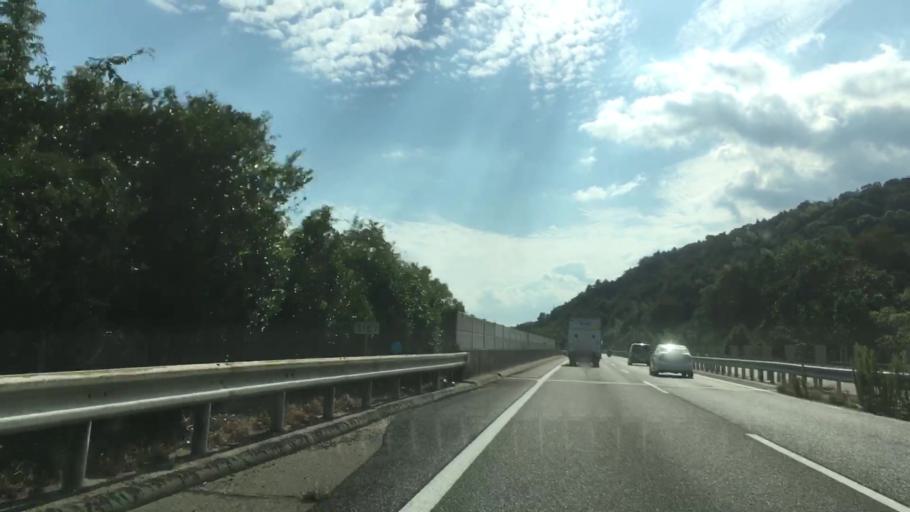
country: JP
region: Hiroshima
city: Ono-hara
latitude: 34.2864
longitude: 132.2638
